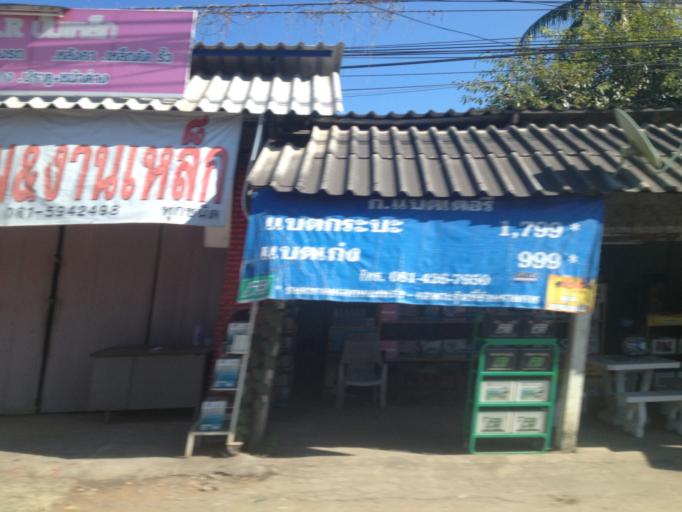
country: TH
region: Chiang Mai
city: Hang Dong
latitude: 18.6793
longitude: 98.9178
